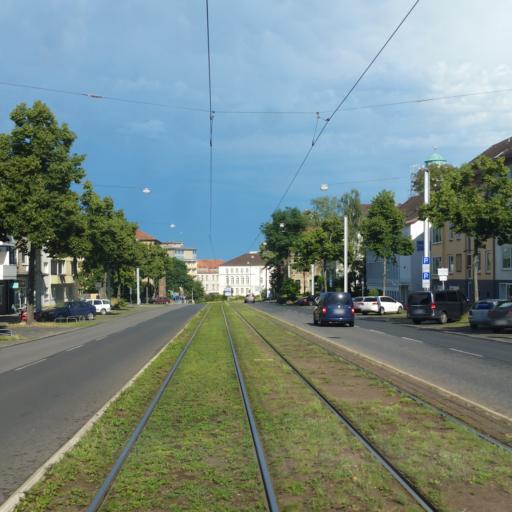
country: DE
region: Hesse
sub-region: Regierungsbezirk Kassel
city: Kassel
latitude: 51.3115
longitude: 9.4873
